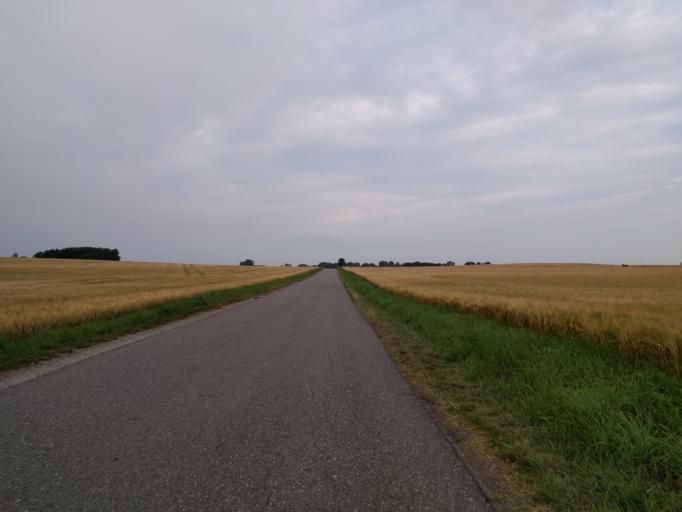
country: DK
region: South Denmark
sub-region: Kerteminde Kommune
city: Kerteminde
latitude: 55.4354
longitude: 10.6152
